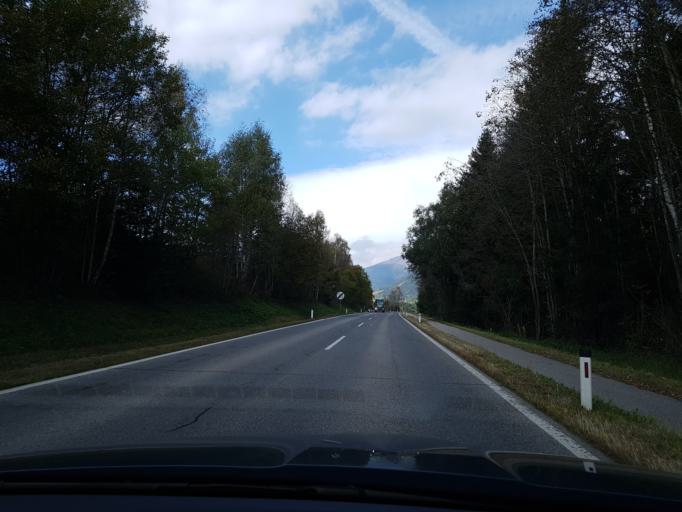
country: AT
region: Carinthia
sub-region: Politischer Bezirk Feldkirchen
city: Gnesau
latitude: 46.7924
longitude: 13.9226
